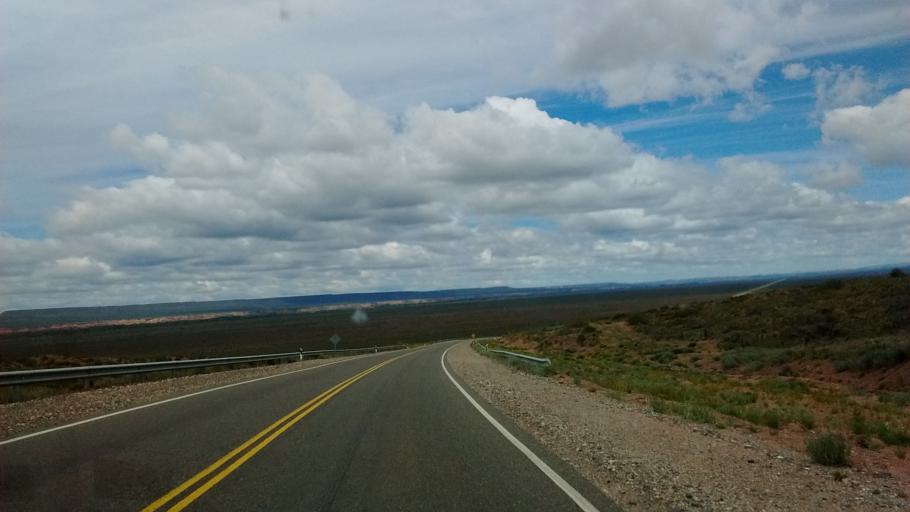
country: AR
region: Neuquen
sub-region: Departamento de Picun Leufu
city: Picun Leufu
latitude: -39.7797
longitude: -69.6551
